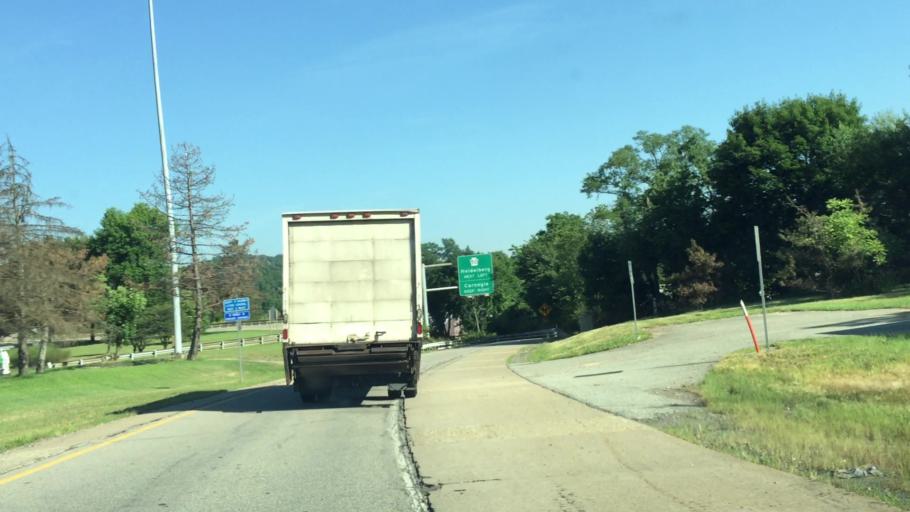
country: US
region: Pennsylvania
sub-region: Allegheny County
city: Carnegie
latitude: 40.4118
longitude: -80.0759
